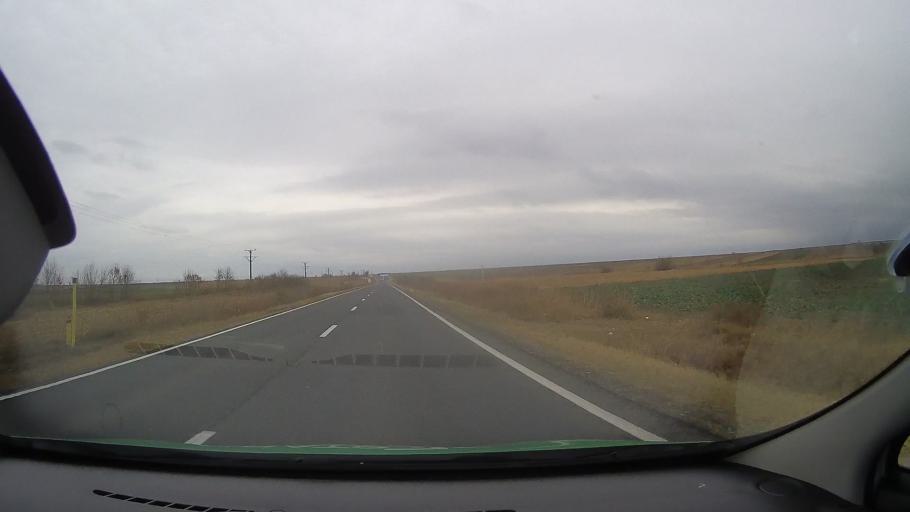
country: RO
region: Constanta
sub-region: Comuna Nicolae Balcescu
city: Nicolae Balcescu
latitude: 44.3848
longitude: 28.3944
